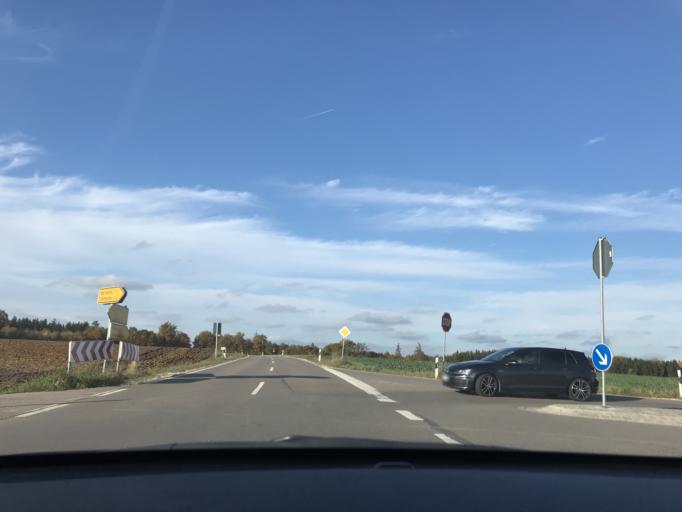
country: DE
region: Bavaria
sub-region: Lower Bavaria
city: Bad Abbach
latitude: 48.9445
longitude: 12.0847
